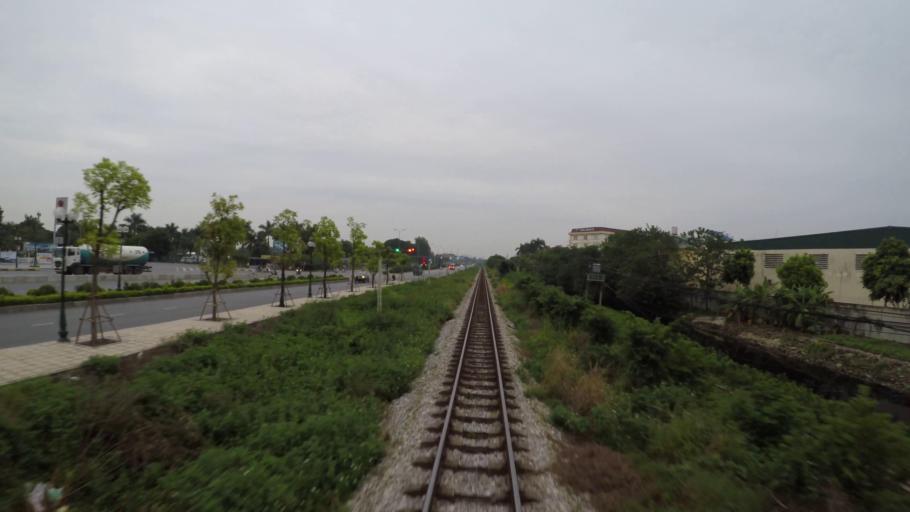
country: VN
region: Ha Noi
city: Trau Quy
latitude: 21.0148
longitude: 105.9470
